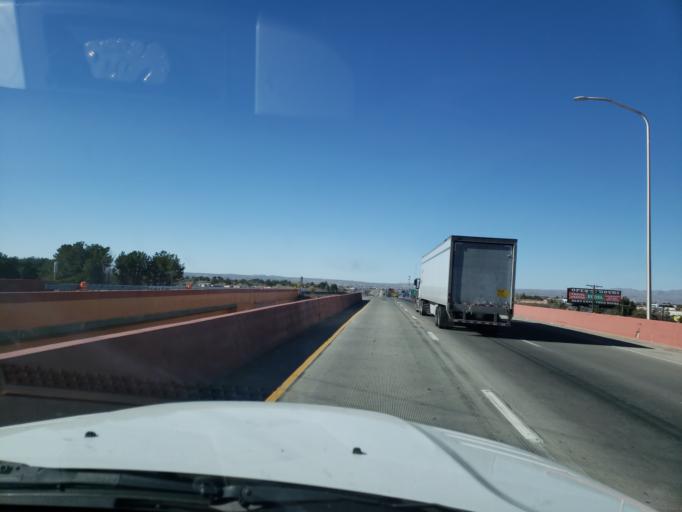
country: US
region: New Mexico
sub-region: Dona Ana County
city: University Park
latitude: 32.2813
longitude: -106.7704
